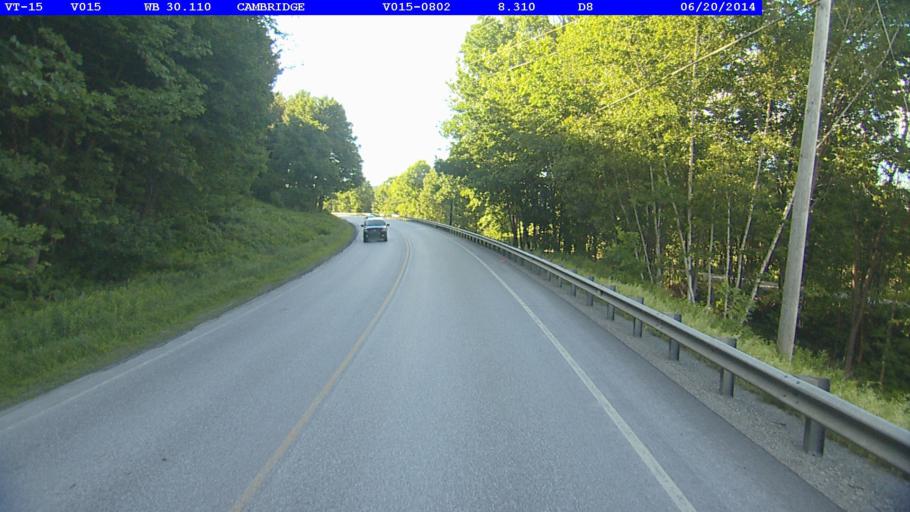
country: US
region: Vermont
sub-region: Lamoille County
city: Johnson
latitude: 44.6650
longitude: -72.7756
